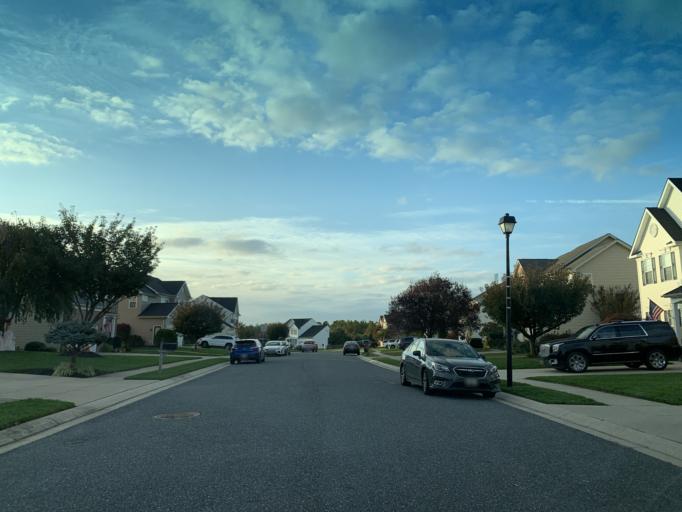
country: US
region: Maryland
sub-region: Harford County
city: South Bel Air
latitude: 39.5380
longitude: -76.3124
